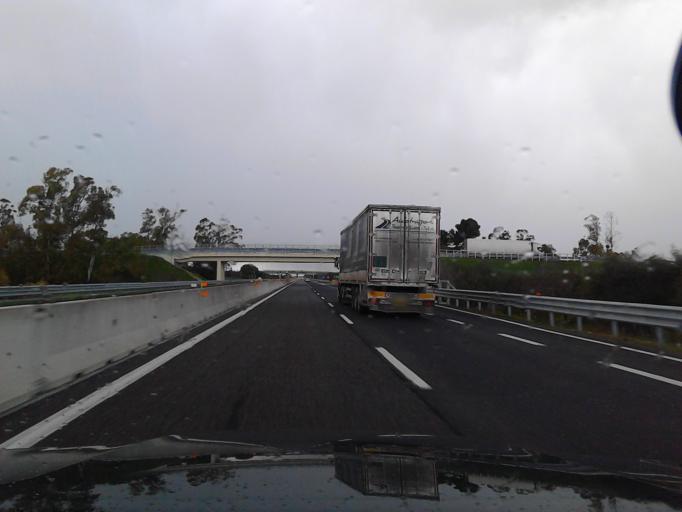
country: IT
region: Apulia
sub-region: Provincia di Bari
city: Bitonto
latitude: 41.1402
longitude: 16.6920
